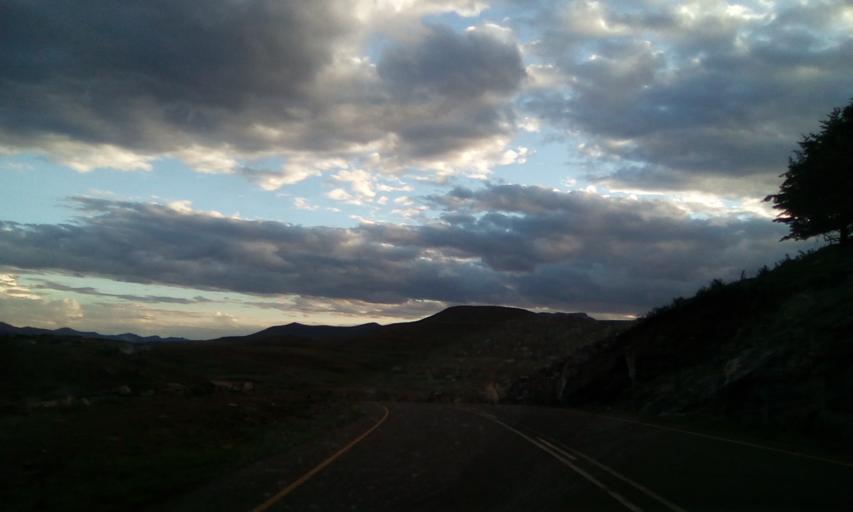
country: LS
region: Maseru
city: Nako
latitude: -29.8014
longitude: 28.0326
